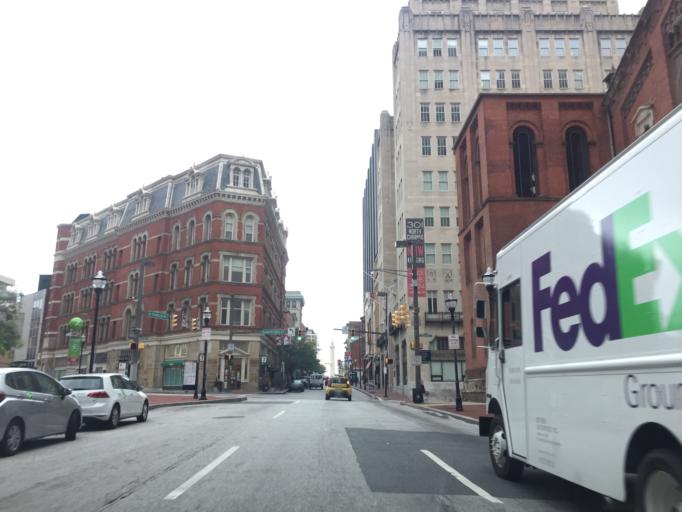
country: US
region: Maryland
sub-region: City of Baltimore
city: Baltimore
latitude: 39.2919
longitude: -76.6153
